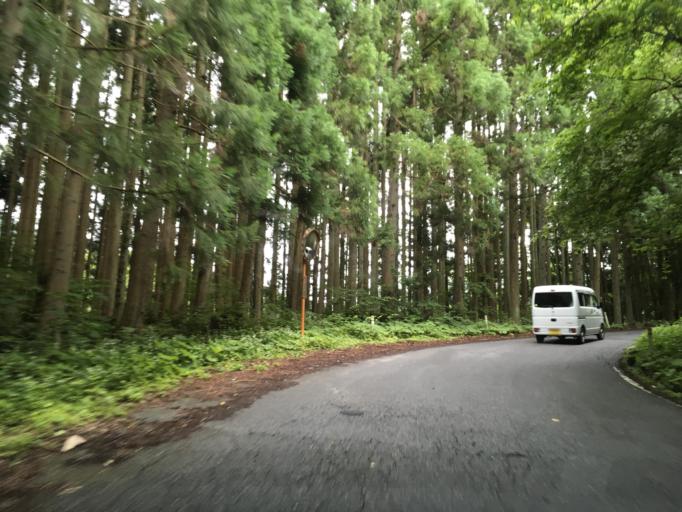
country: JP
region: Iwate
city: Ofunato
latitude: 38.8828
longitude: 141.4700
